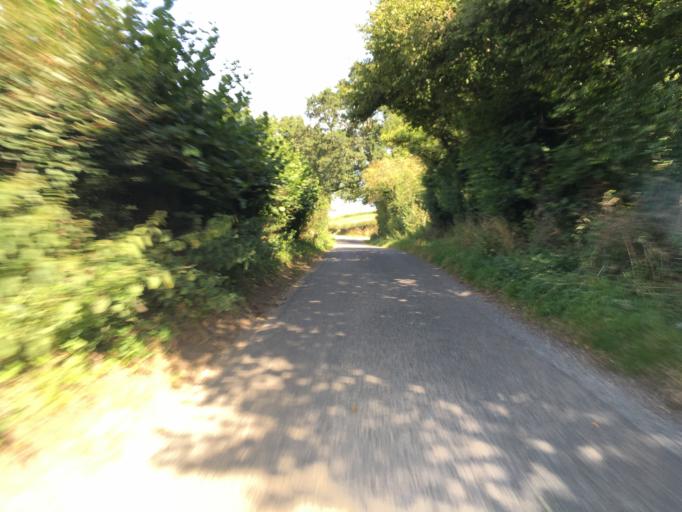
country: GB
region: England
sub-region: Hampshire
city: Highclere
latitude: 51.2843
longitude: -1.3594
